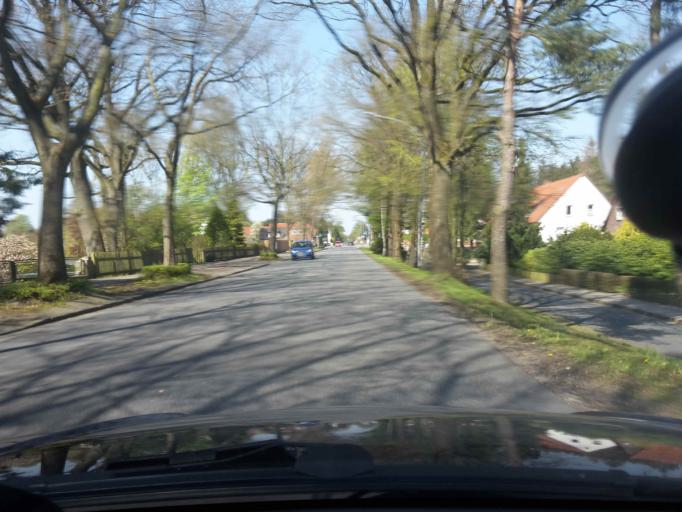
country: DE
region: Lower Saxony
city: Schneverdingen
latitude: 53.1099
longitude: 9.8071
